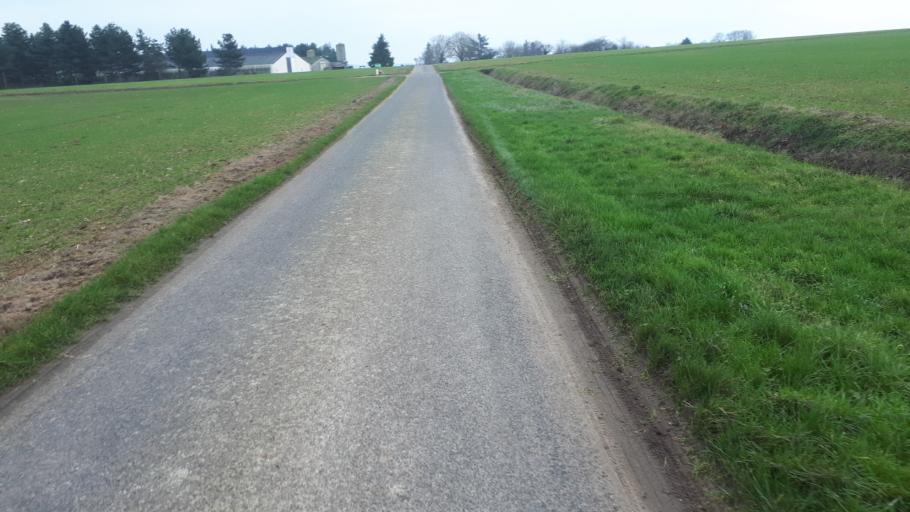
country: FR
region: Centre
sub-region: Departement du Loir-et-Cher
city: Villiers-sur-Loir
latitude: 47.8161
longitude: 0.9967
